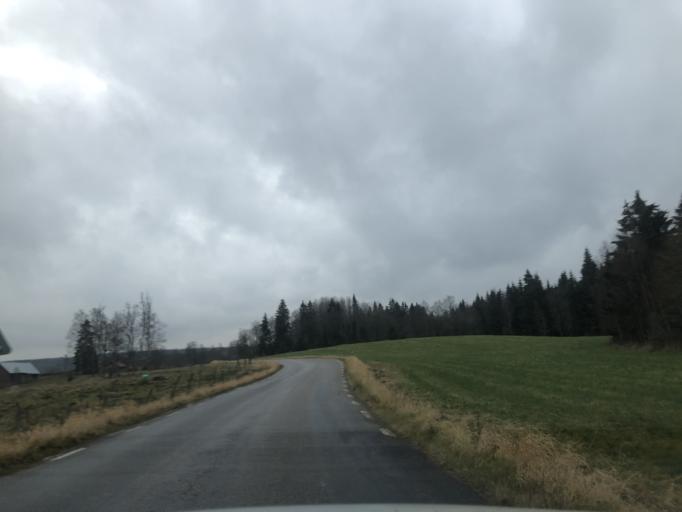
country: SE
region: Vaestra Goetaland
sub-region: Ulricehamns Kommun
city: Ulricehamn
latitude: 57.8925
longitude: 13.5101
